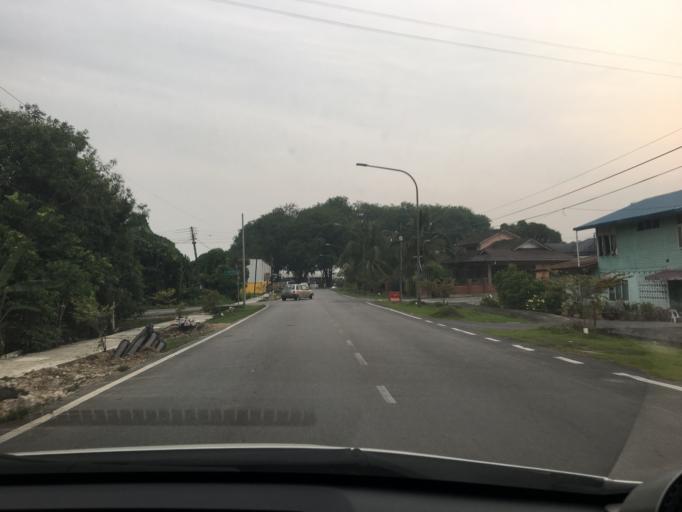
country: MY
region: Sarawak
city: Kuching
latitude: 1.5562
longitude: 110.3278
